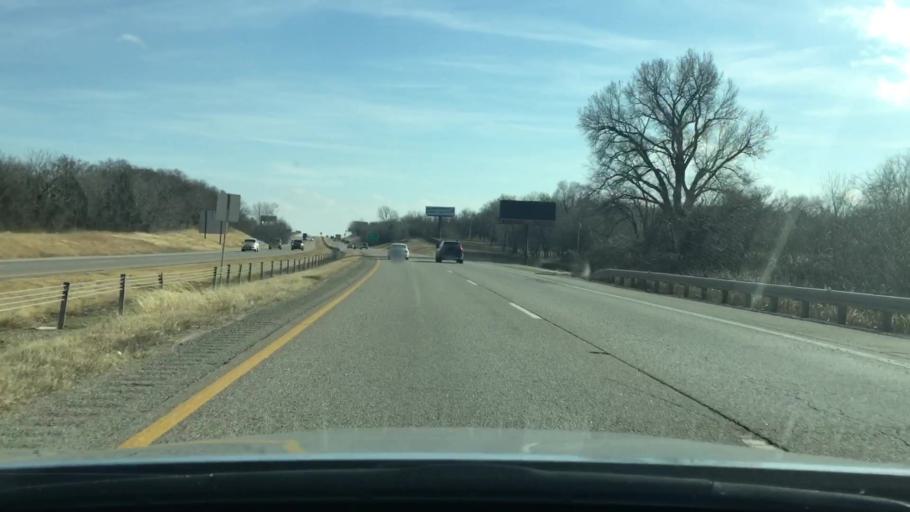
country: US
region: Oklahoma
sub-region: McClain County
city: Goldsby
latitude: 35.1692
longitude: -97.4917
